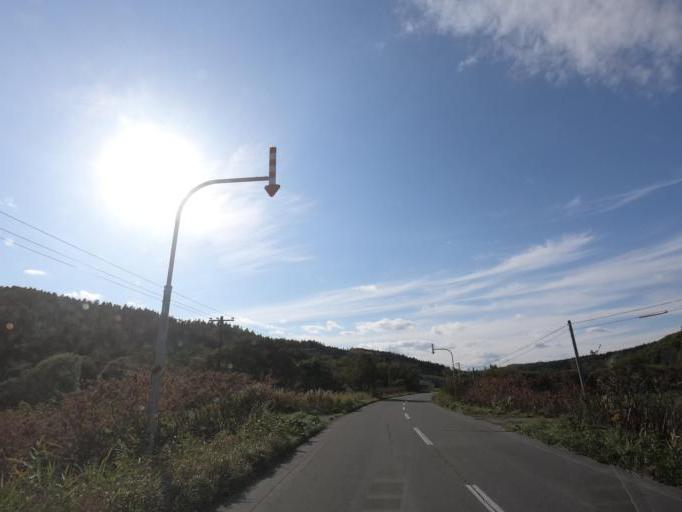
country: JP
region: Hokkaido
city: Obihiro
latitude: 42.6172
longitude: 143.4160
